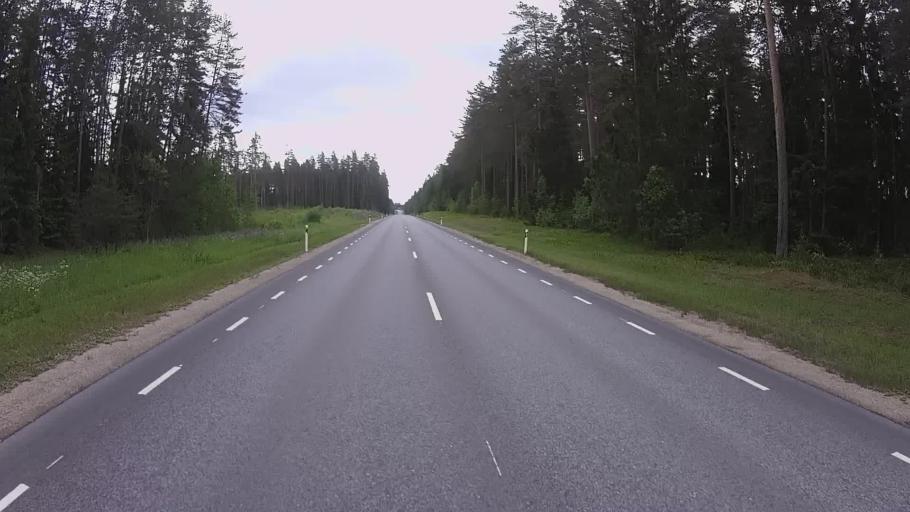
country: EE
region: Polvamaa
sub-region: Polva linn
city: Polva
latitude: 58.1045
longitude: 26.9915
